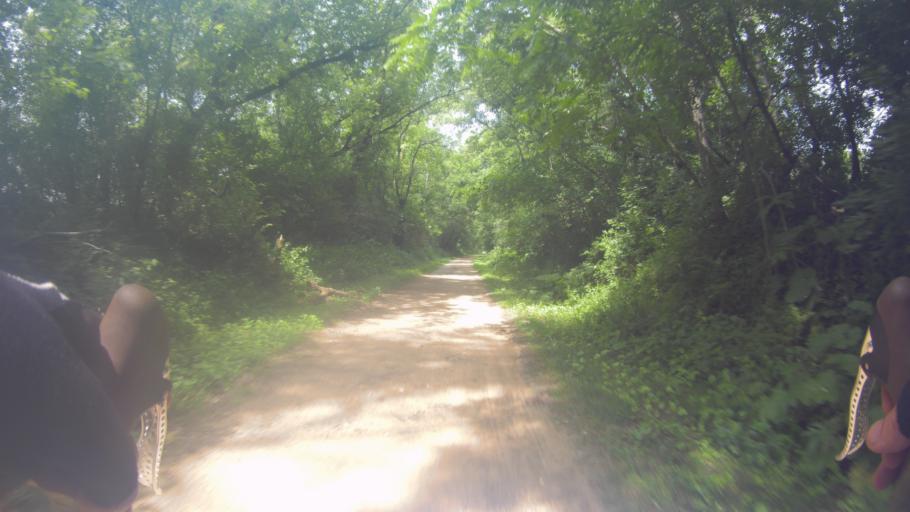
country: US
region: Wisconsin
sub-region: Dane County
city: Mount Horeb
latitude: 43.0164
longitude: -89.6884
